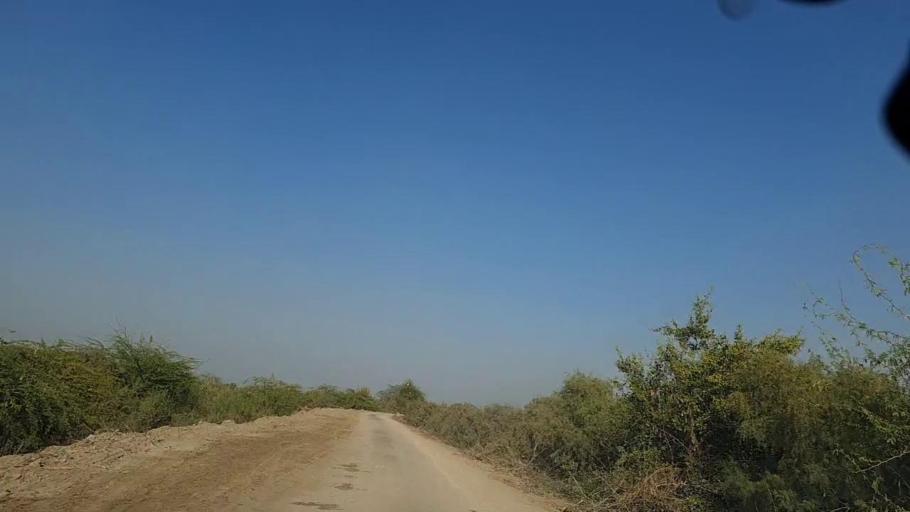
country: PK
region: Sindh
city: Mirpur Khas
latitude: 25.5135
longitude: 68.9302
